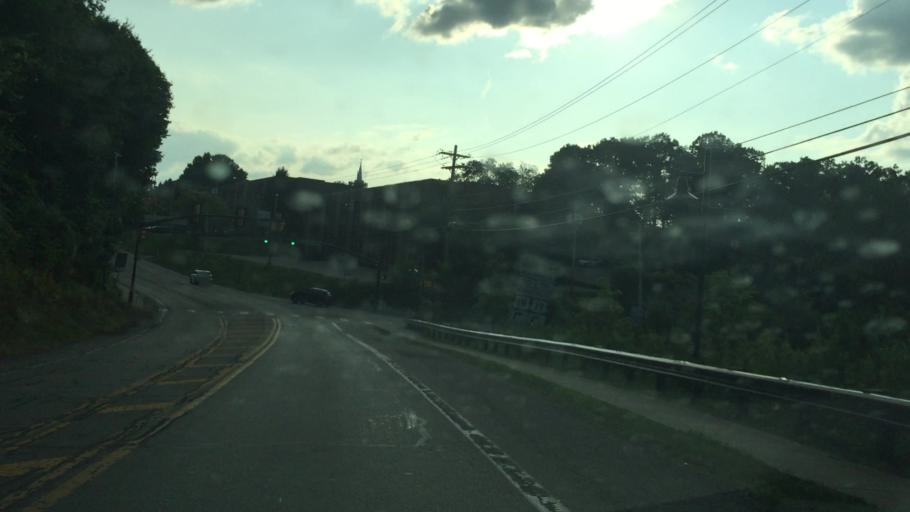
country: US
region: Pennsylvania
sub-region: Allegheny County
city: Bradford Woods
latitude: 40.6275
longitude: -80.0515
